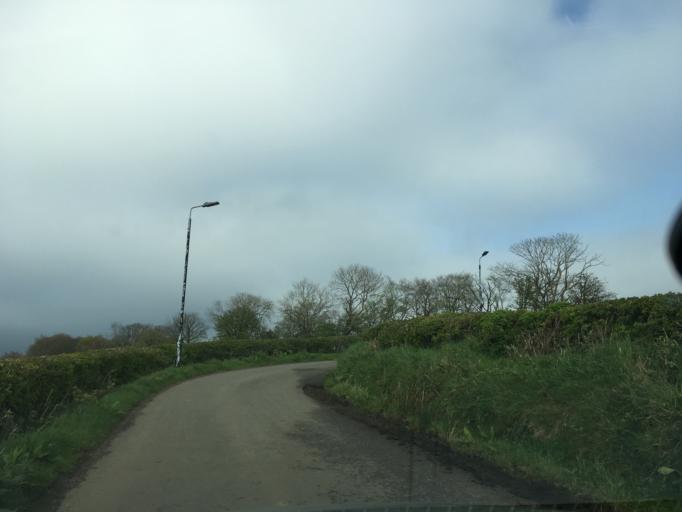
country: GB
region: Scotland
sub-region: Argyll and Bute
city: Rothesay
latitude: 55.8353
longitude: -5.0426
